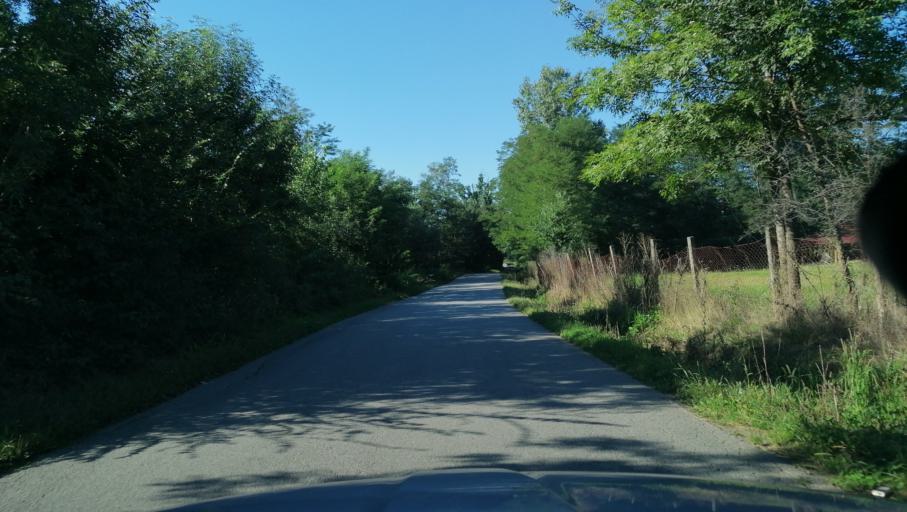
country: RS
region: Central Serbia
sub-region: Sumadijski Okrug
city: Knic
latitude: 43.8574
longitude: 20.6015
